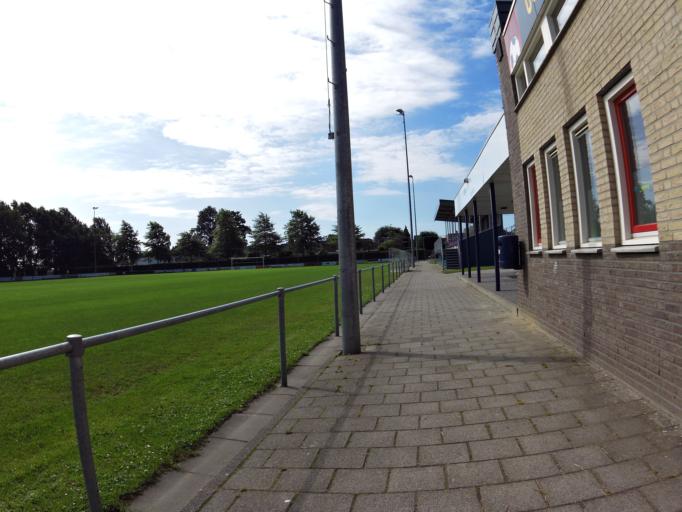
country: NL
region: Limburg
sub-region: Gemeente Kerkrade
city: Kerkrade
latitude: 50.9166
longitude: 6.0575
